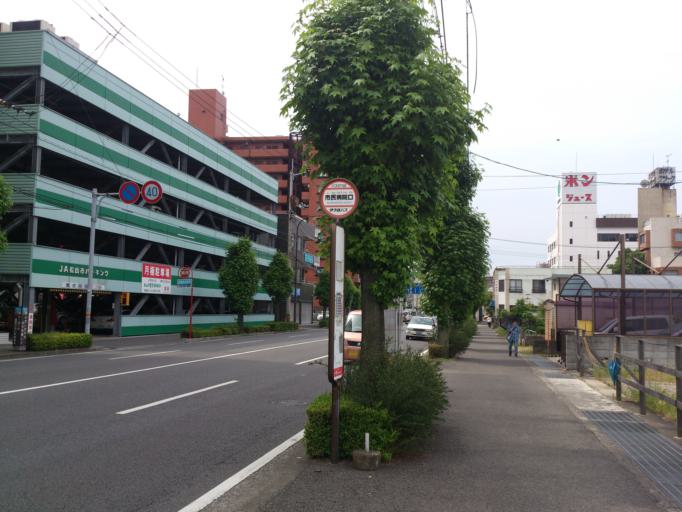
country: JP
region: Ehime
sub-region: Shikoku-chuo Shi
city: Matsuyama
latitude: 33.8383
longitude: 132.7524
